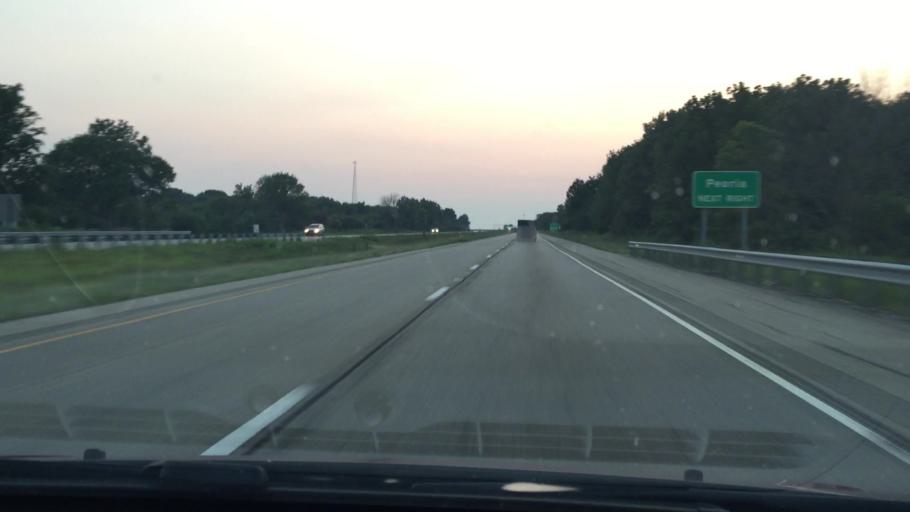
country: US
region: Illinois
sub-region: Bureau County
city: Depue
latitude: 41.4000
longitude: -89.3616
